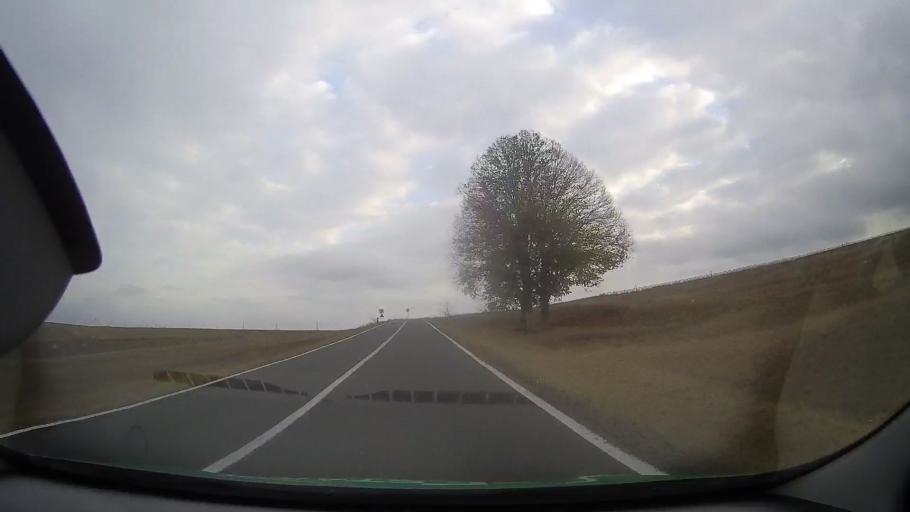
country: RO
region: Constanta
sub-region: Comuna Deleni
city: Deleni
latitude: 44.0947
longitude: 28.0166
